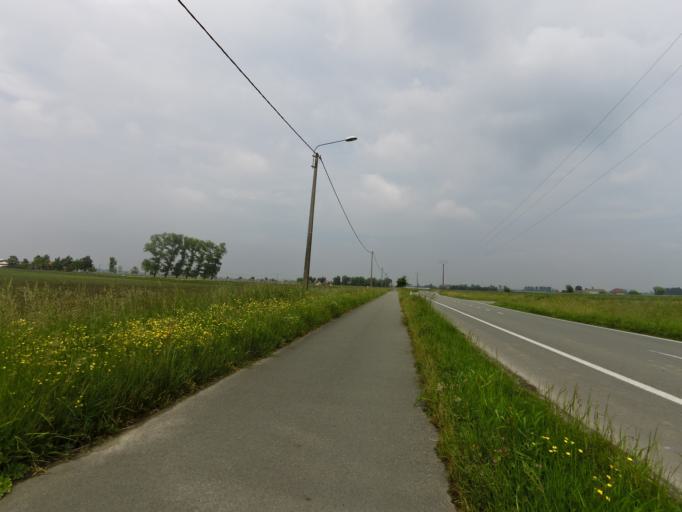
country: BE
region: Flanders
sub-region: Provincie West-Vlaanderen
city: Koekelare
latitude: 51.0981
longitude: 2.9113
